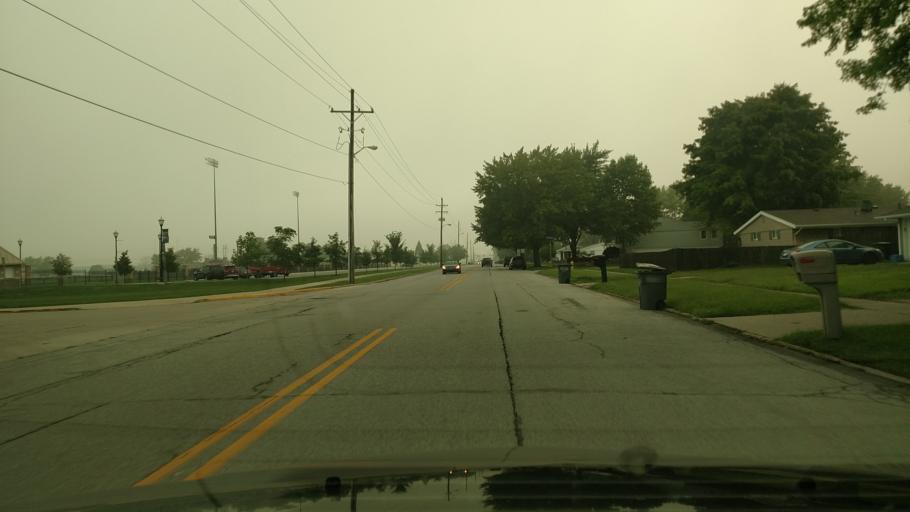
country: US
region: Indiana
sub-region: Howard County
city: Kokomo
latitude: 40.4570
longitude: -86.1555
